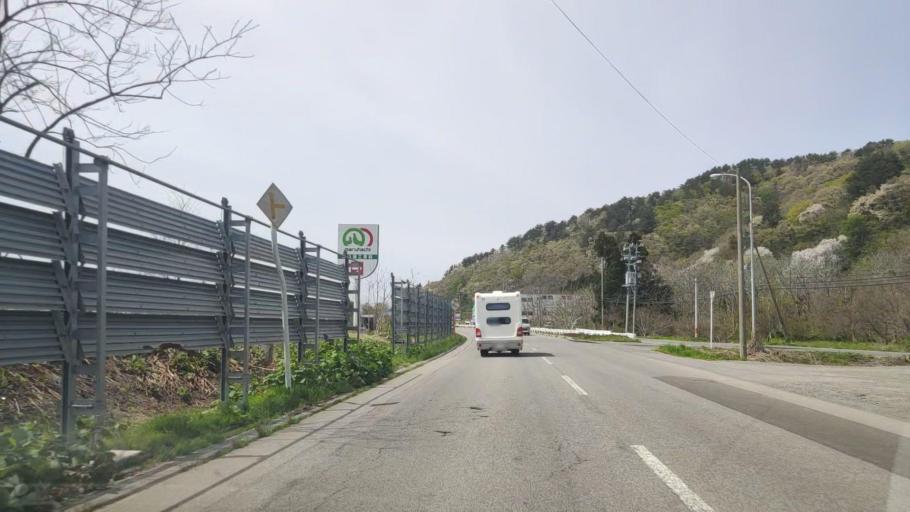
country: JP
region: Aomori
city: Aomori Shi
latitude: 40.8292
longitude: 140.8511
